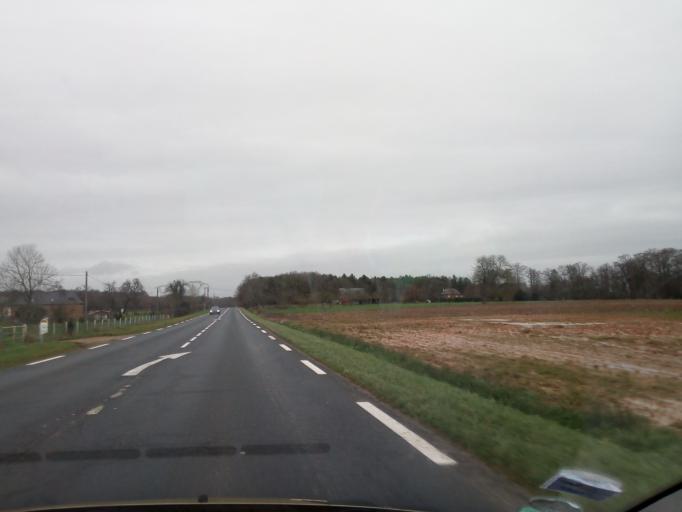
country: FR
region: Haute-Normandie
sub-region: Departement de l'Eure
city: Hauville
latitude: 49.4088
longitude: 0.7969
